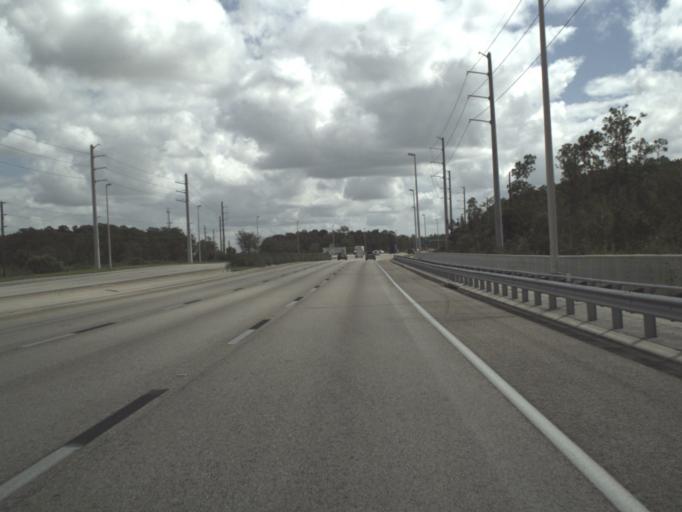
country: US
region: Florida
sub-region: Lee County
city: Tice
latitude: 26.6283
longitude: -81.7819
